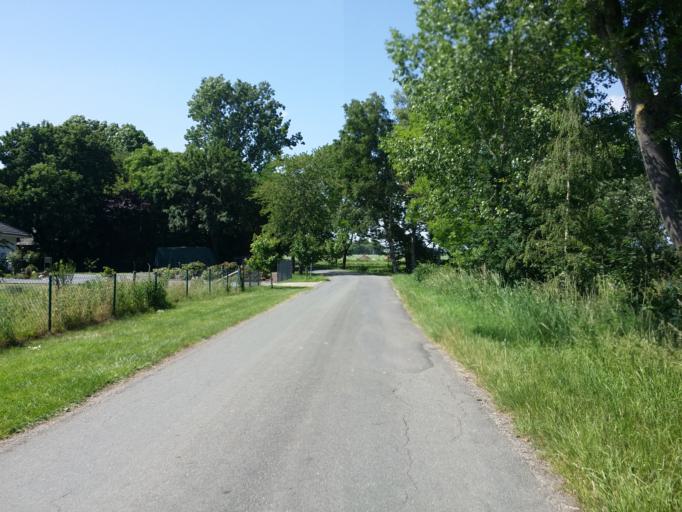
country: DE
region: Lower Saxony
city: Lemwerder
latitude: 53.1518
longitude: 8.5471
